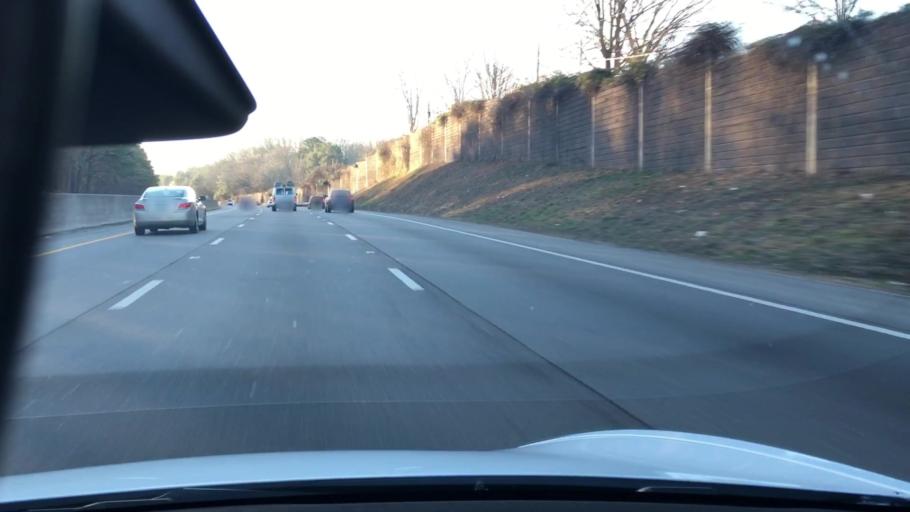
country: US
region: Virginia
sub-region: Chesterfield County
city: Bon Air
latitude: 37.4724
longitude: -77.5122
